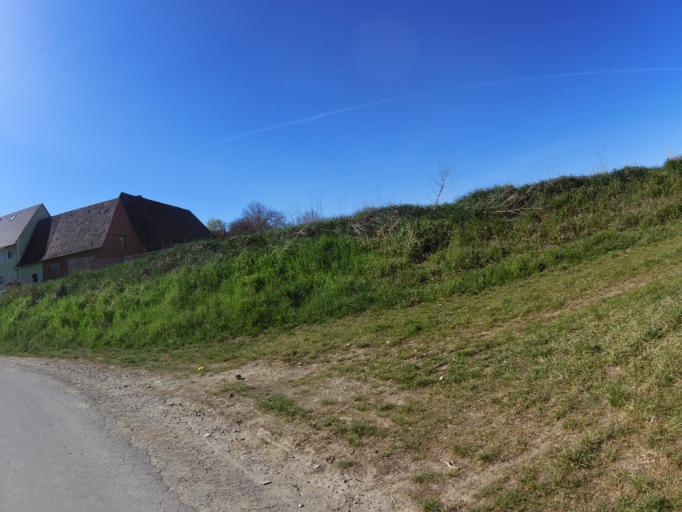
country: DE
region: Bavaria
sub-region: Regierungsbezirk Unterfranken
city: Rottendorf
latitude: 49.8115
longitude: 10.0597
